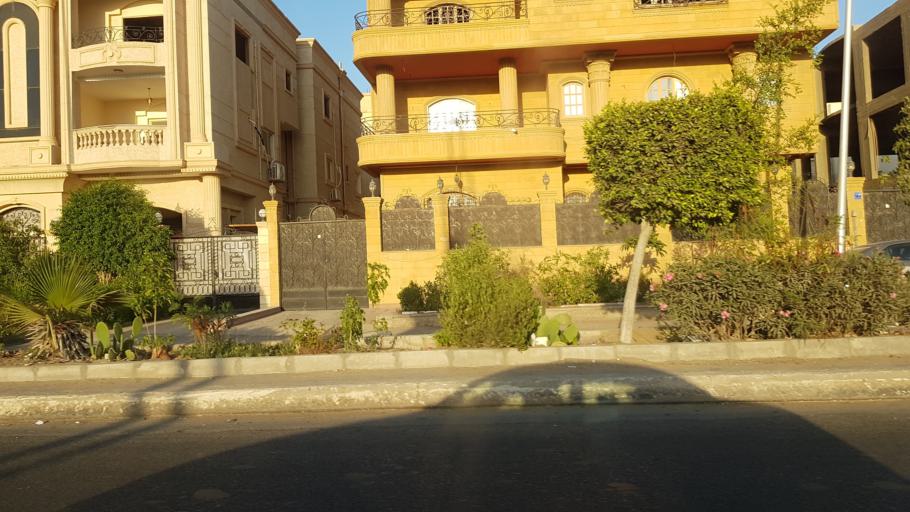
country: EG
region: Muhafazat al Qalyubiyah
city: Al Khankah
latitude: 30.0548
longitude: 31.4426
